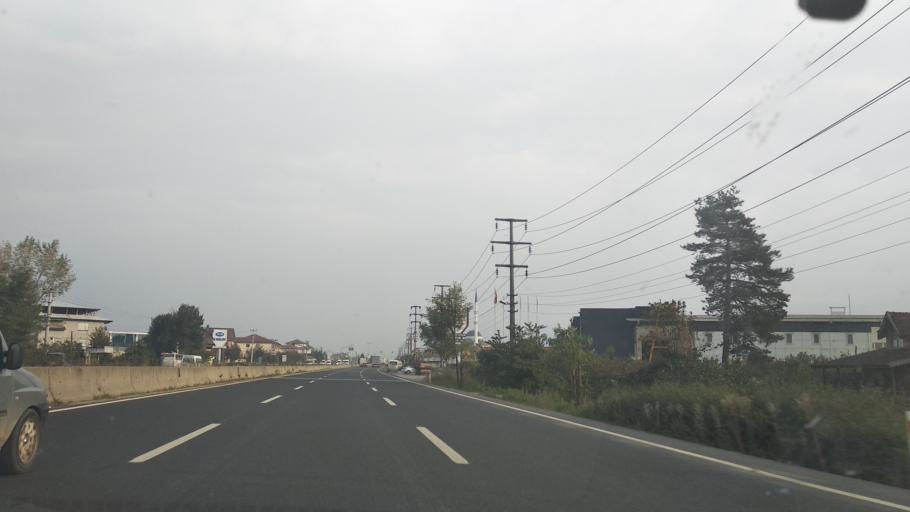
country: TR
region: Duzce
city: Duzce
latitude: 40.8055
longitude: 31.2330
